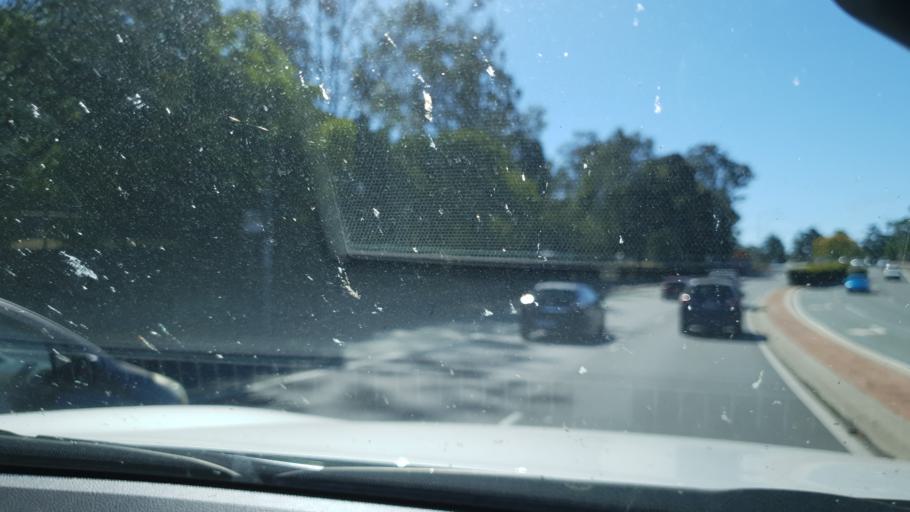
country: AU
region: Queensland
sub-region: Brisbane
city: Bridegman Downs
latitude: -27.3573
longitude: 152.9696
